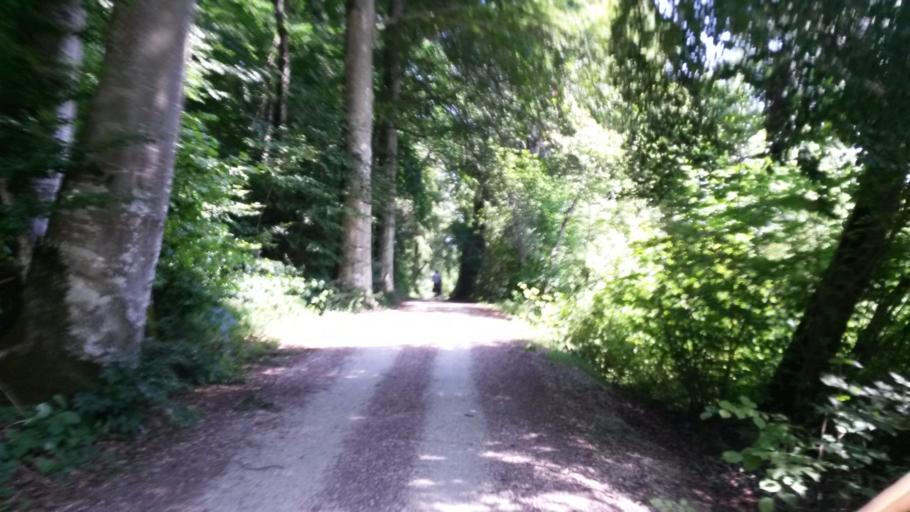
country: DE
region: Bavaria
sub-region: Upper Bavaria
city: Gstadt am Chiemsee
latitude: 47.9062
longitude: 12.4323
